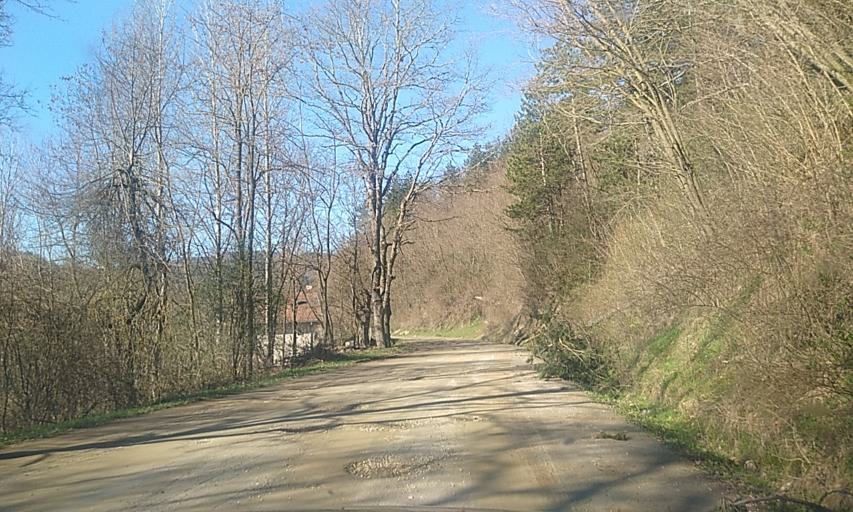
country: RS
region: Central Serbia
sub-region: Pcinjski Okrug
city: Bosilegrad
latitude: 42.3680
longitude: 22.4354
